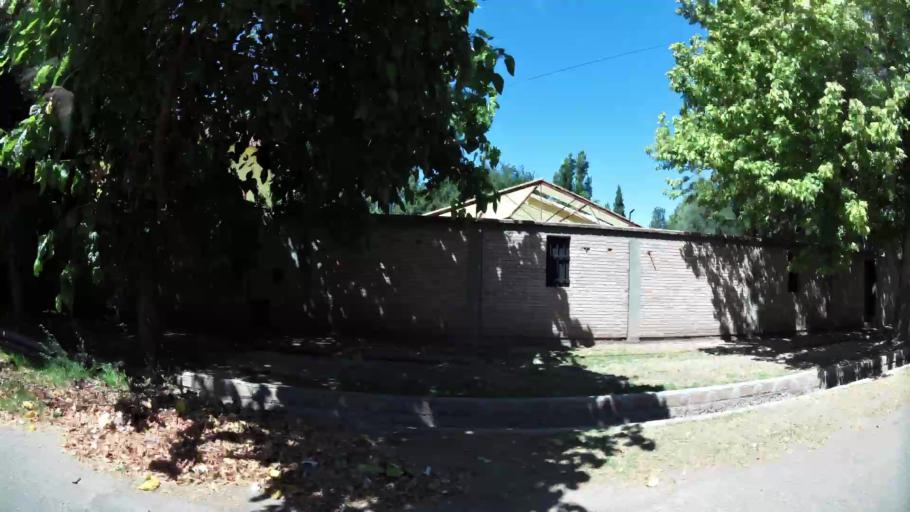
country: AR
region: Mendoza
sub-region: Departamento de Godoy Cruz
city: Godoy Cruz
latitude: -32.9702
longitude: -68.8721
